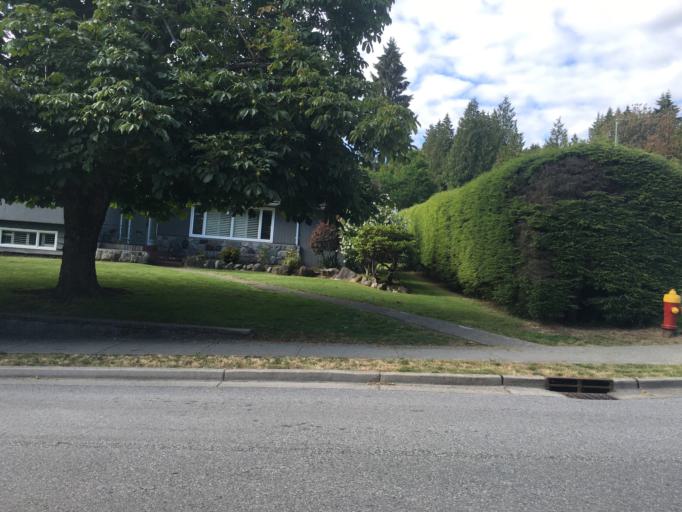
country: CA
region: British Columbia
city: Port Moody
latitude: 49.2454
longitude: -122.8774
